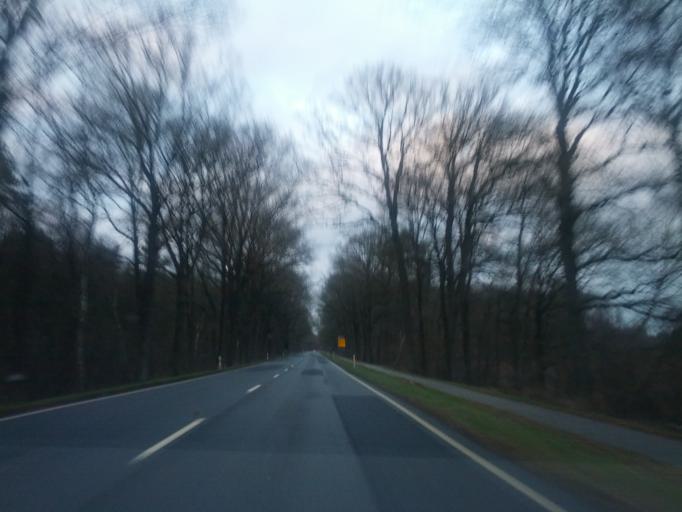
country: DE
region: Lower Saxony
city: Stemmen
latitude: 53.2407
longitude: 9.6050
